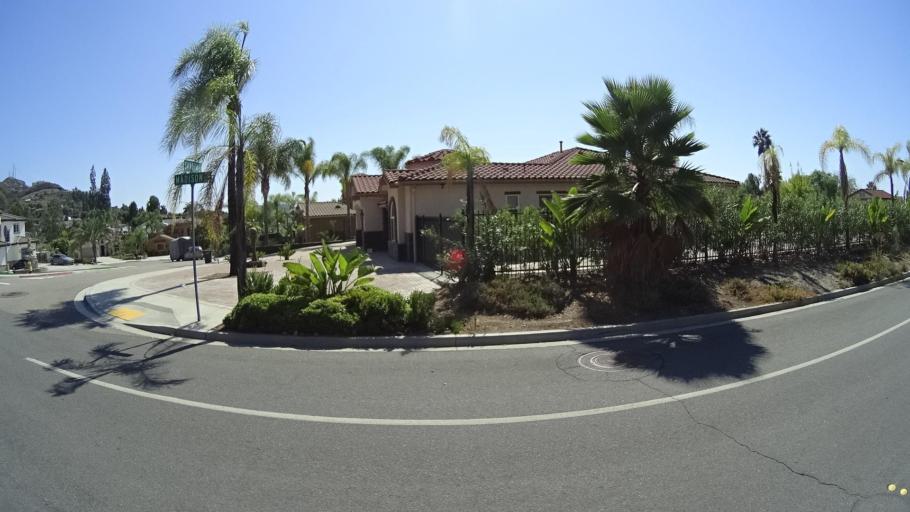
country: US
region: California
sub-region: San Diego County
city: Granite Hills
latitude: 32.8031
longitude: -116.9000
